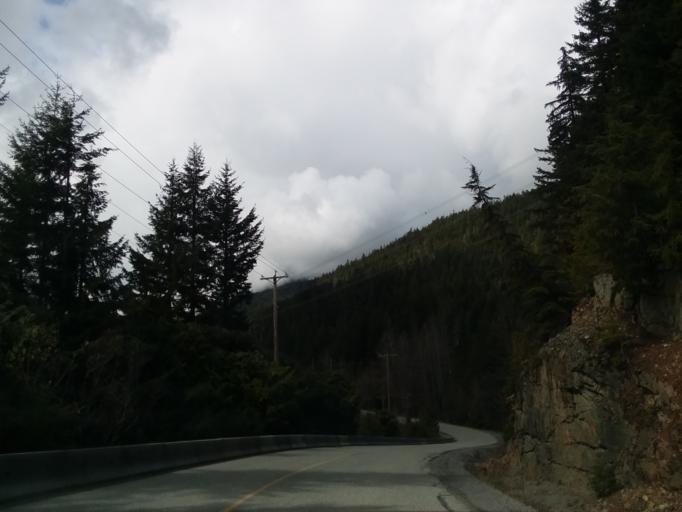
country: CA
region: British Columbia
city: Whistler
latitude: 50.0945
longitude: -123.0075
